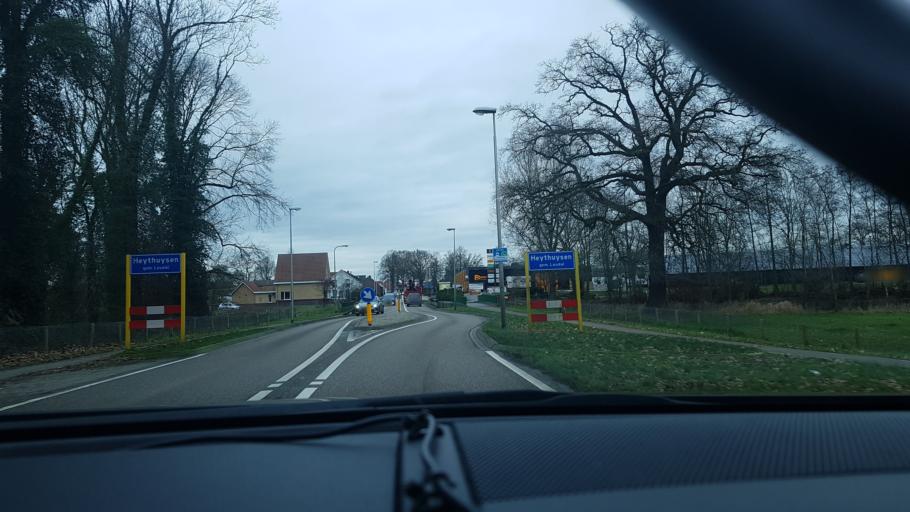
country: NL
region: Limburg
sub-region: Gemeente Leudal
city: Heythuysen
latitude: 51.2412
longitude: 5.9043
